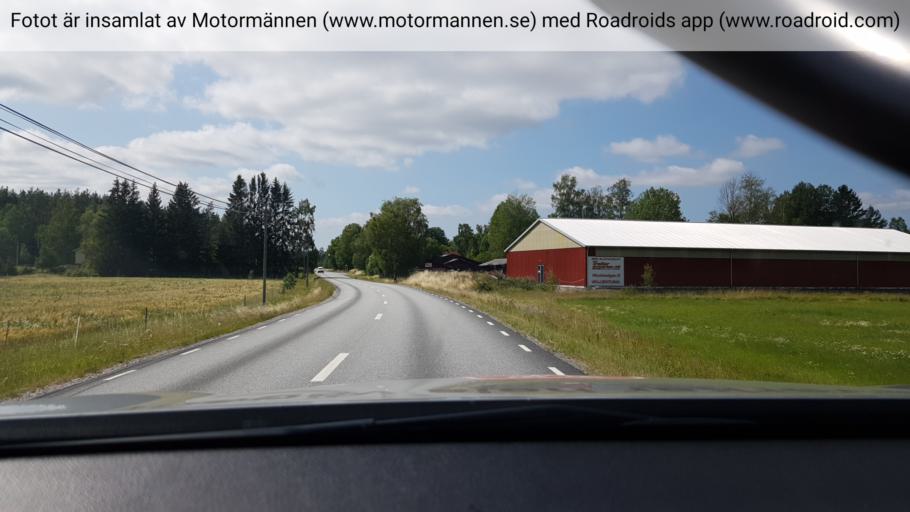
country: SE
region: Stockholm
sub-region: Osterakers Kommun
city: Akersberga
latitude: 59.5473
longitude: 18.2006
